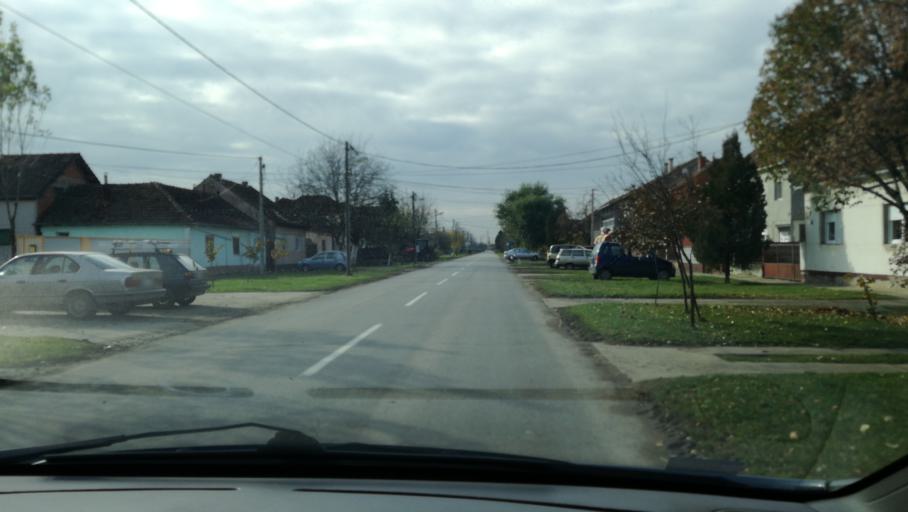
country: RS
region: Autonomna Pokrajina Vojvodina
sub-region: Severnobanatski Okrug
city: Kikinda
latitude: 45.8281
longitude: 20.4362
